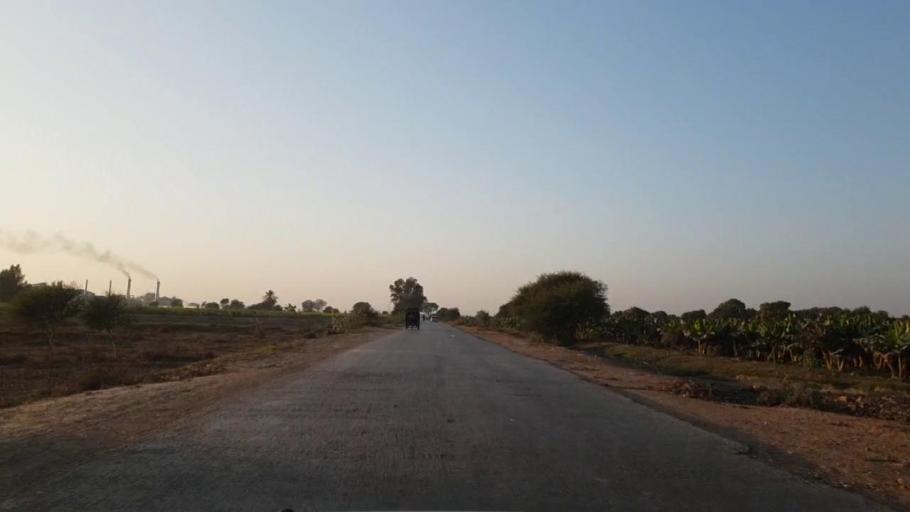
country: PK
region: Sindh
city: Chambar
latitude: 25.2477
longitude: 68.6808
